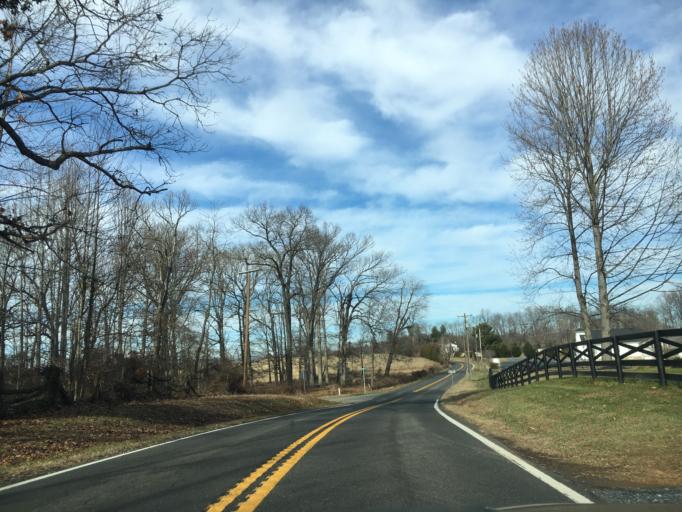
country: US
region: Virginia
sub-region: Fauquier County
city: Marshall
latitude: 38.7427
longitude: -77.9605
